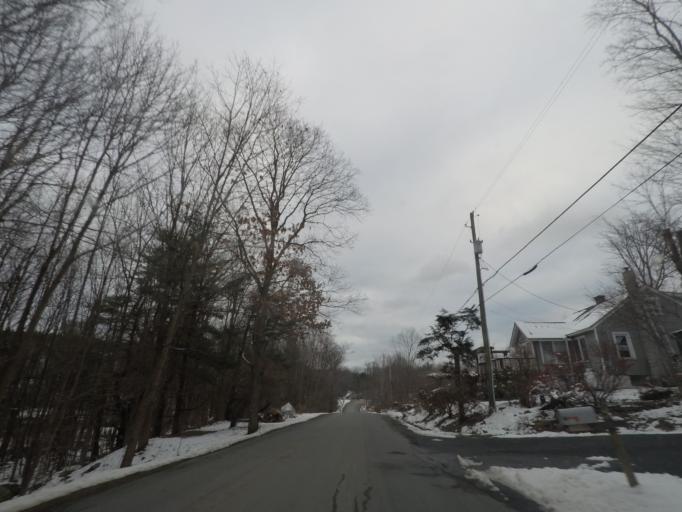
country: US
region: New York
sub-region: Rensselaer County
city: Averill Park
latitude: 42.6403
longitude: -73.5378
